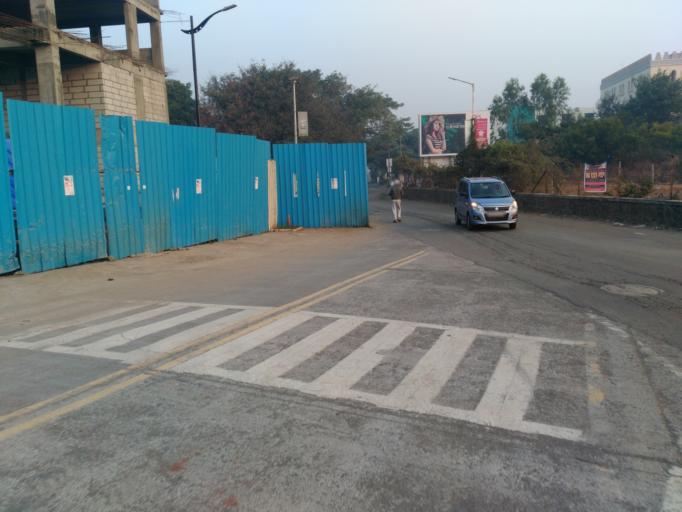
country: IN
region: Maharashtra
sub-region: Pune Division
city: Pune
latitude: 18.4439
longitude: 73.8857
